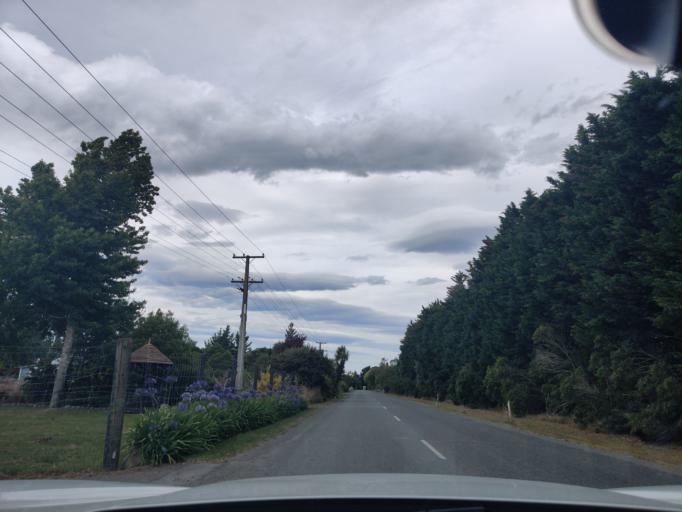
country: NZ
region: Wellington
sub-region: Masterton District
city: Masterton
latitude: -41.0414
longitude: 175.5036
